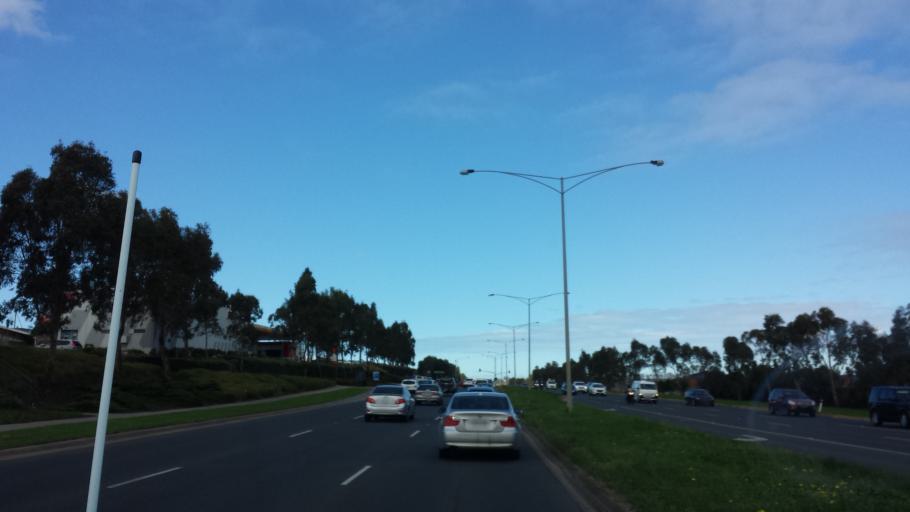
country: AU
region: Victoria
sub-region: Casey
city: Berwick
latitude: -38.0602
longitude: 145.3383
